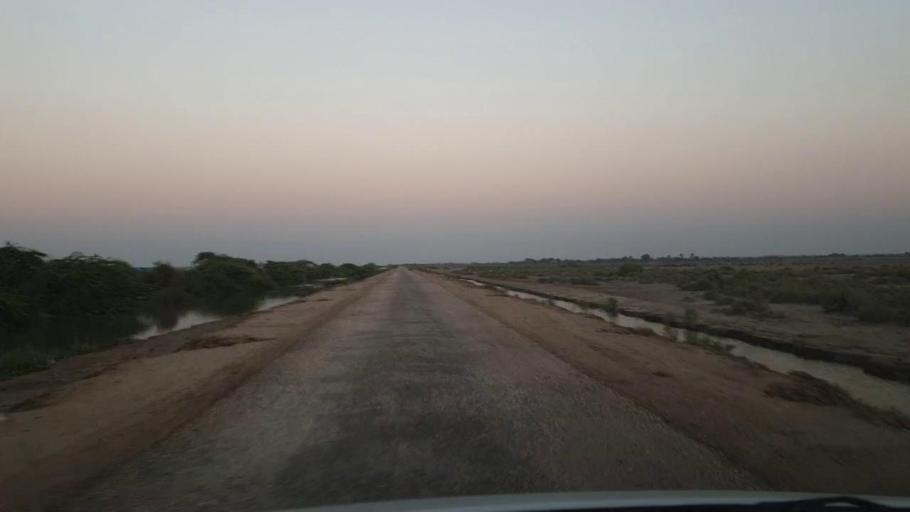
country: PK
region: Sindh
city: Mirpur Sakro
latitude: 24.3852
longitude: 67.5709
